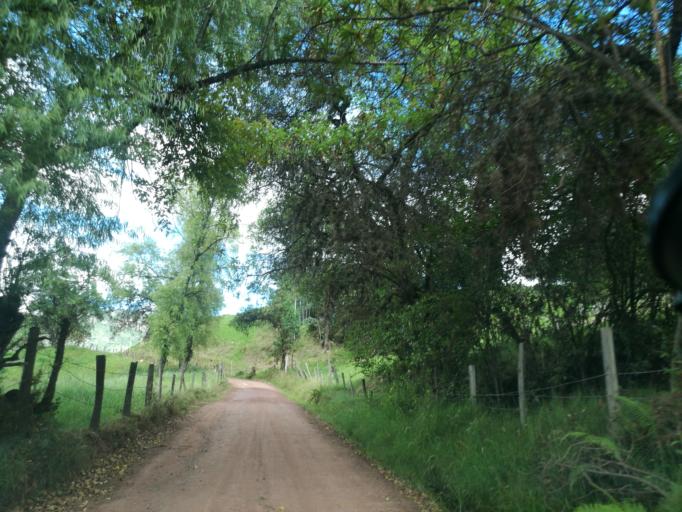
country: CO
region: Boyaca
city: Socota
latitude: 6.1119
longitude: -72.7180
